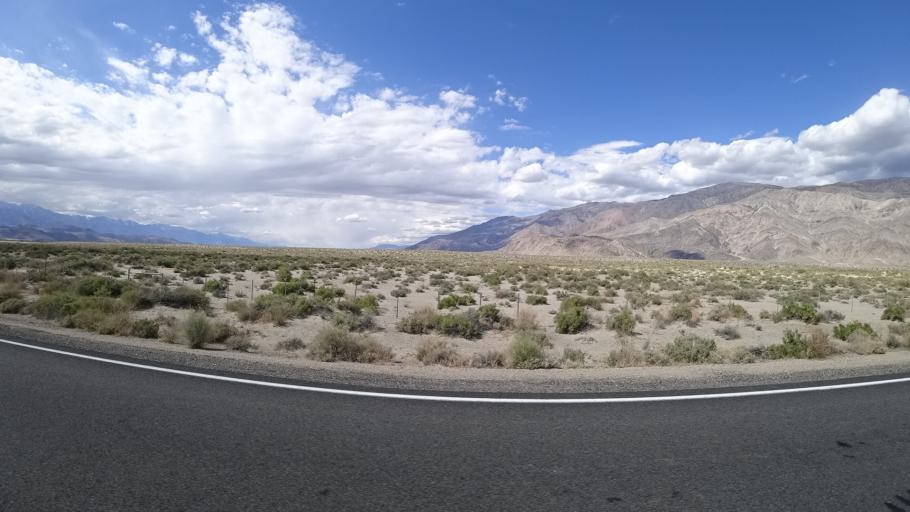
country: US
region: California
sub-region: Inyo County
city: Lone Pine
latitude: 36.5742
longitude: -118.0056
